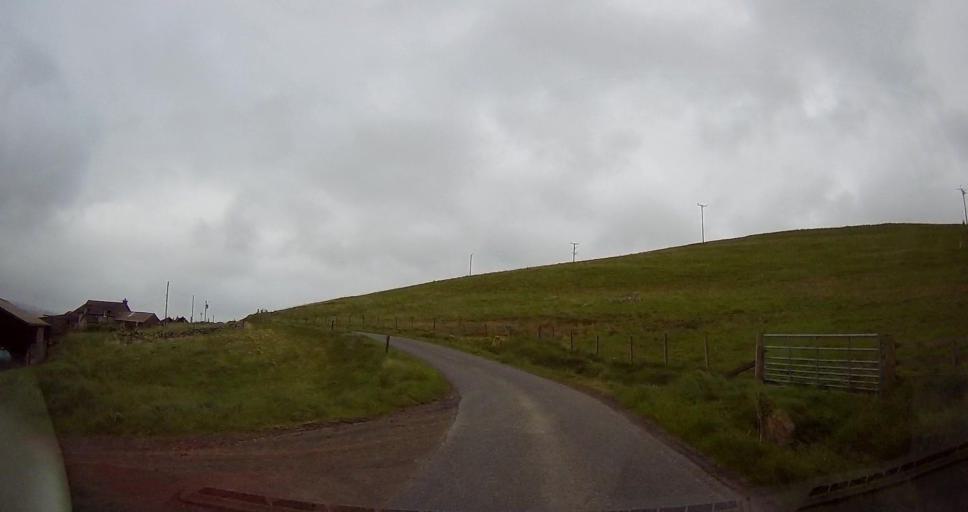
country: GB
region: Scotland
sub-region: Shetland Islands
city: Lerwick
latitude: 60.3716
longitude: -1.3824
